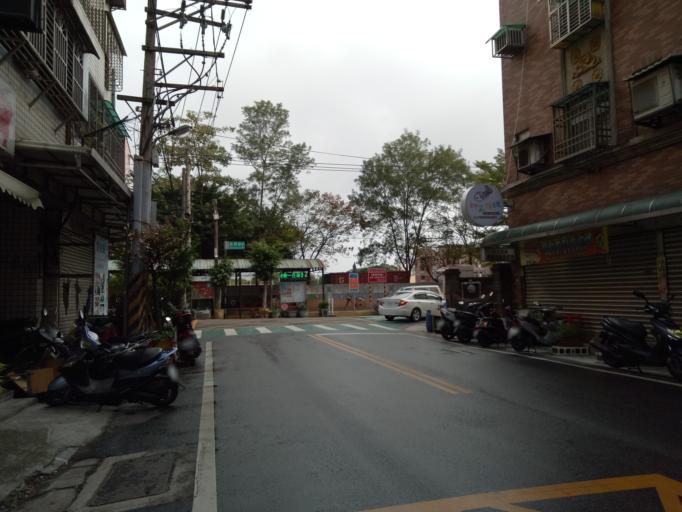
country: TW
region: Taiwan
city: Taoyuan City
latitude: 24.9689
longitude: 121.3031
